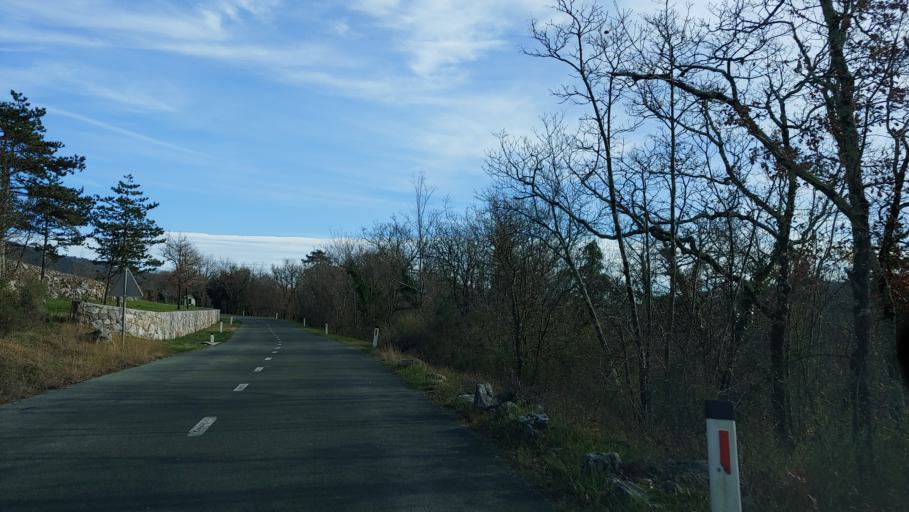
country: IT
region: Friuli Venezia Giulia
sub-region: Provincia di Trieste
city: Sistiana-Visogliano
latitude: 45.8100
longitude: 13.6532
